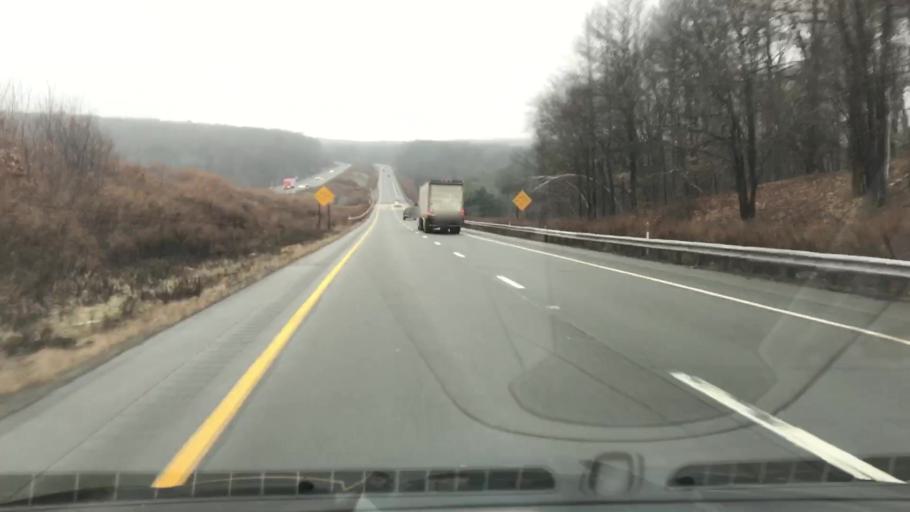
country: US
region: Pennsylvania
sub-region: Pike County
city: Sunrise Lake
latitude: 41.3511
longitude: -74.9611
